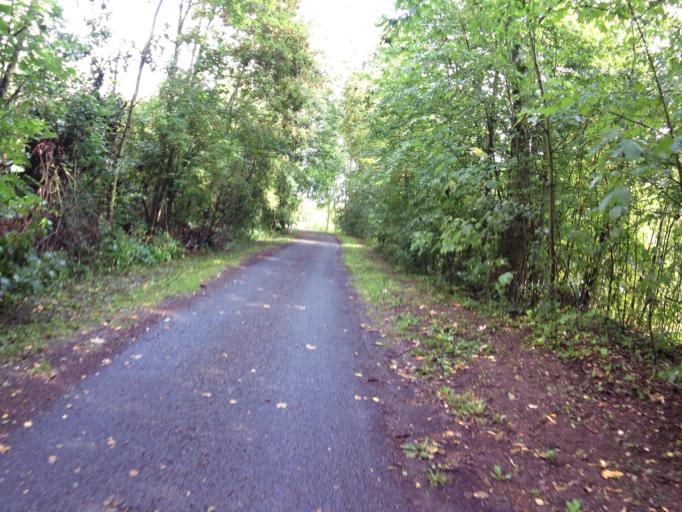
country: DE
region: Lower Saxony
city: Nienburg
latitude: 52.6462
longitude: 9.2041
